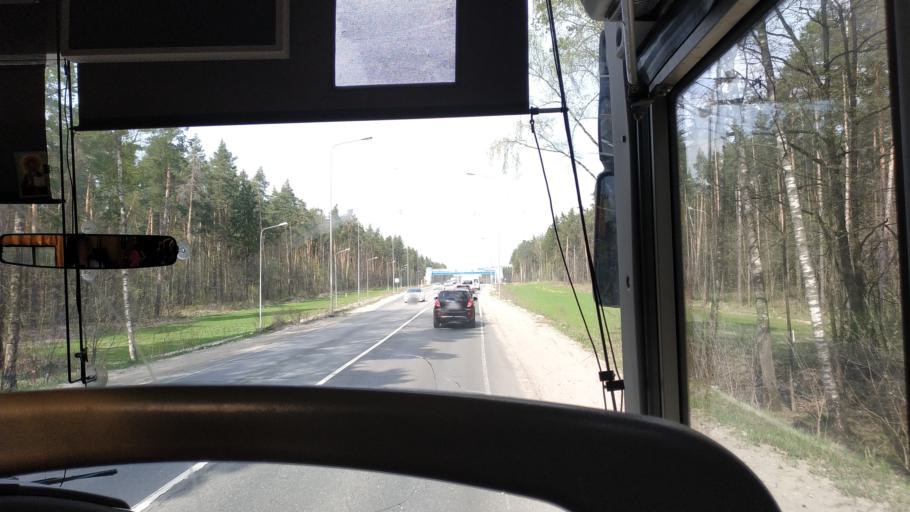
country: RU
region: Moskovskaya
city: Lytkarino
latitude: 55.6105
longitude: 37.9190
